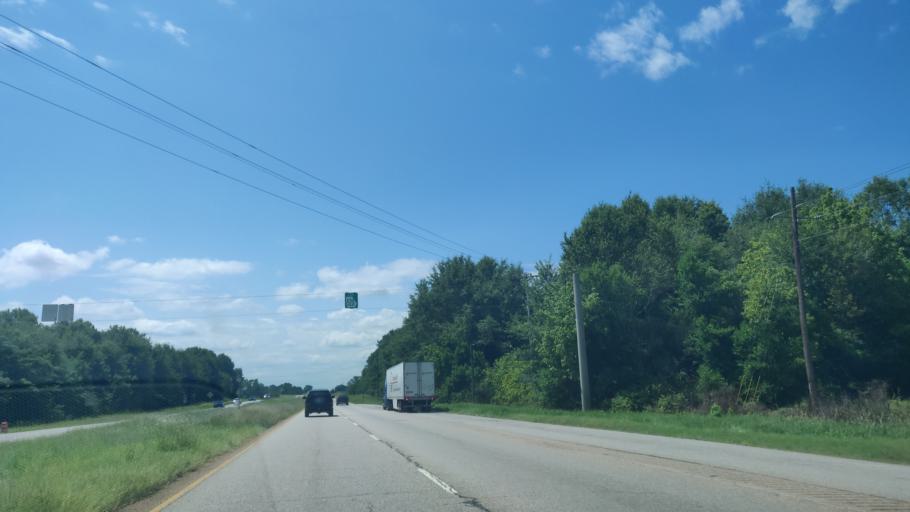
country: US
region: Georgia
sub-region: Stewart County
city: Richland
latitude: 32.0860
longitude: -84.6763
